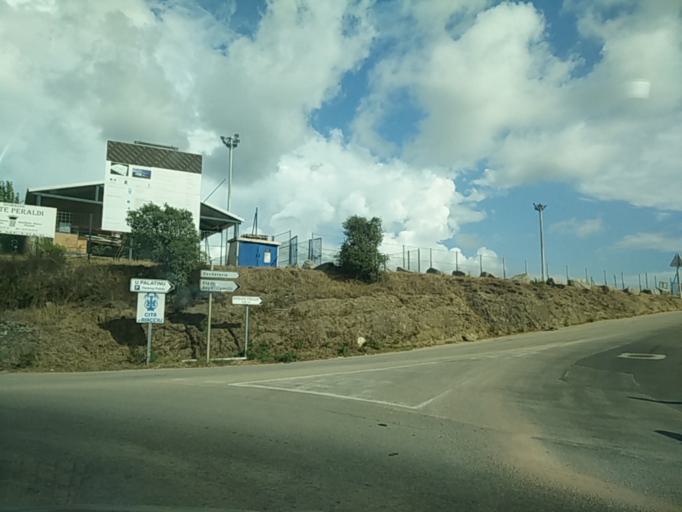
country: FR
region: Corsica
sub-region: Departement de la Corse-du-Sud
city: Ajaccio
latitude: 41.9462
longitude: 8.7722
